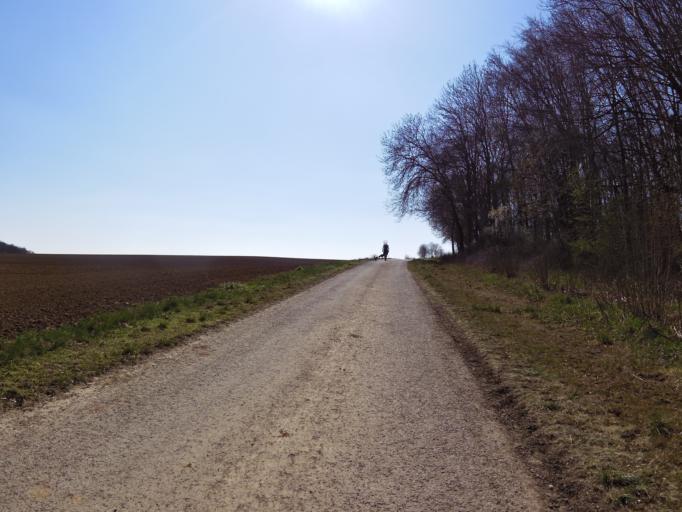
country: DE
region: Bavaria
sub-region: Regierungsbezirk Unterfranken
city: Biebelried
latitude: 49.7745
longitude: 10.0842
